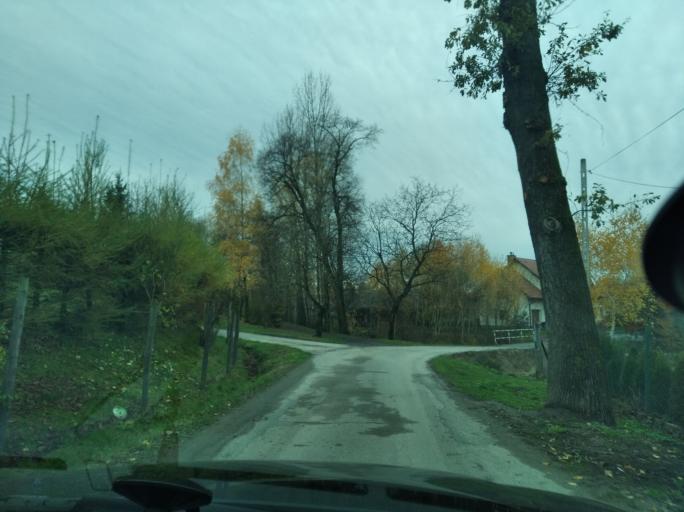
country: PL
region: Subcarpathian Voivodeship
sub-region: Powiat lancucki
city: Markowa
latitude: 50.0207
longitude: 22.3183
